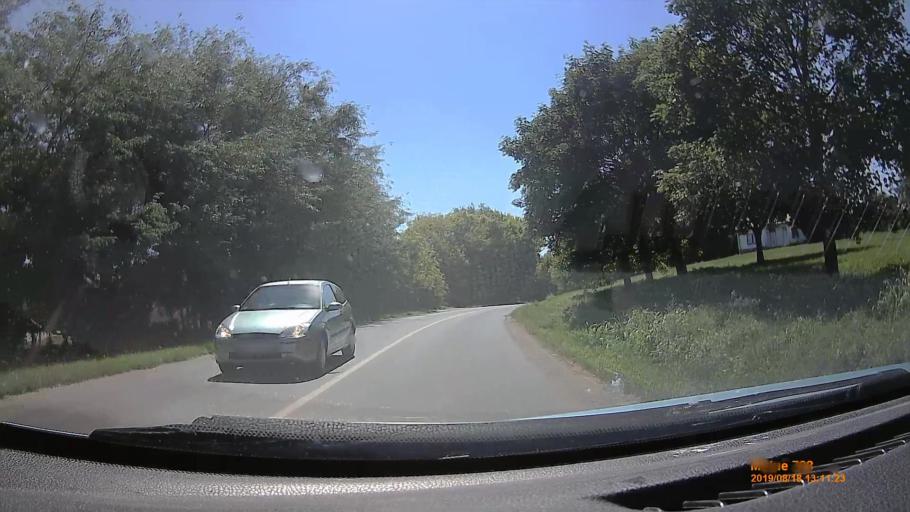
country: HU
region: Fejer
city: Kaloz
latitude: 46.9043
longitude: 18.5192
